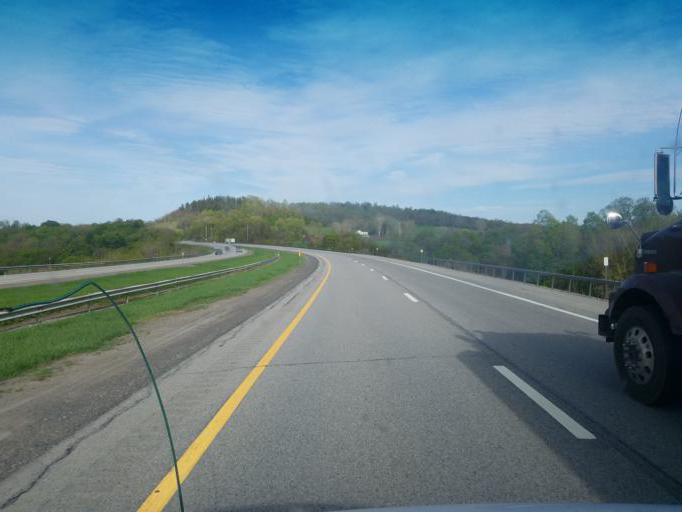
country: US
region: New York
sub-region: Herkimer County
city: Little Falls
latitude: 43.0047
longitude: -74.8873
